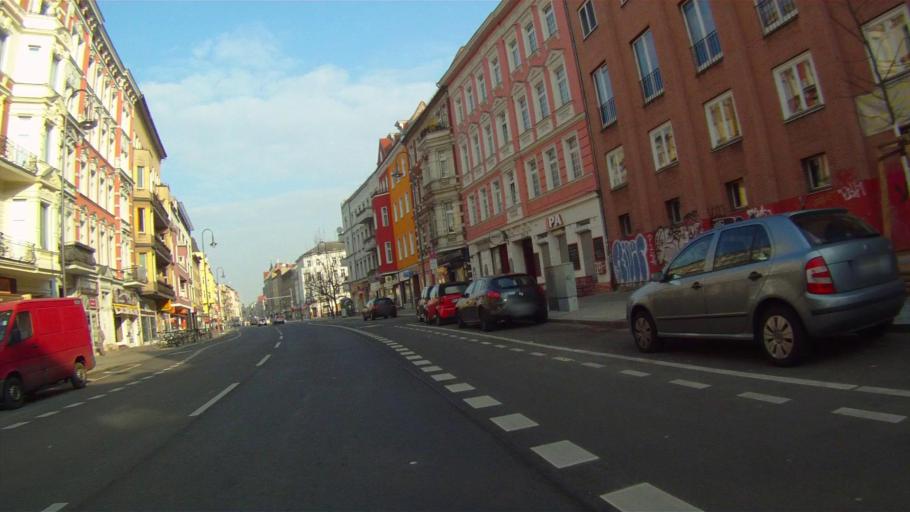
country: DE
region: Berlin
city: Berlin Treptow
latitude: 52.4726
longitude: 13.4412
